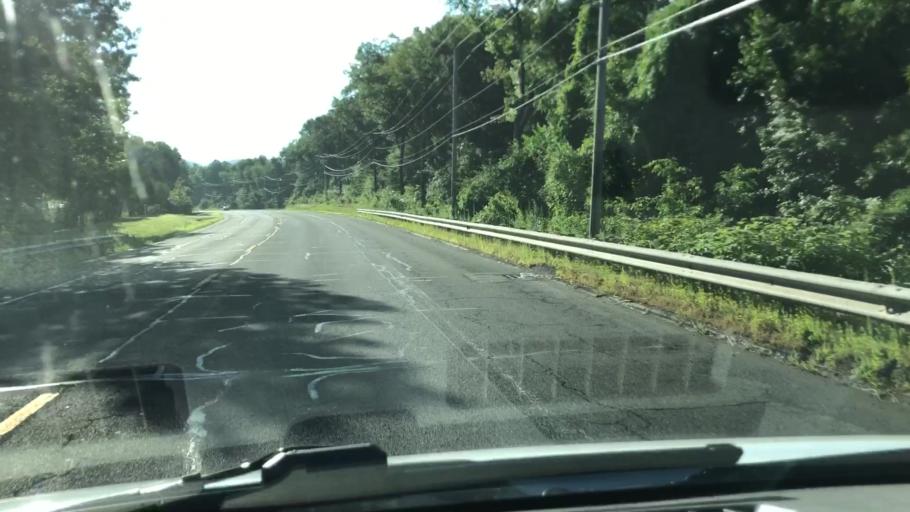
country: US
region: Massachusetts
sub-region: Franklin County
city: South Deerfield
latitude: 42.4673
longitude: -72.6026
